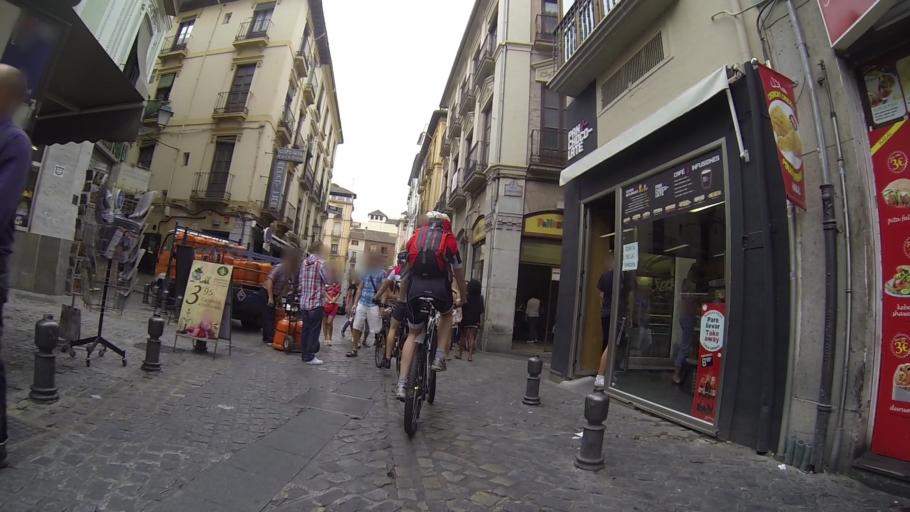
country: ES
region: Andalusia
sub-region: Provincia de Granada
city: Granada
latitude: 37.1773
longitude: -3.5968
